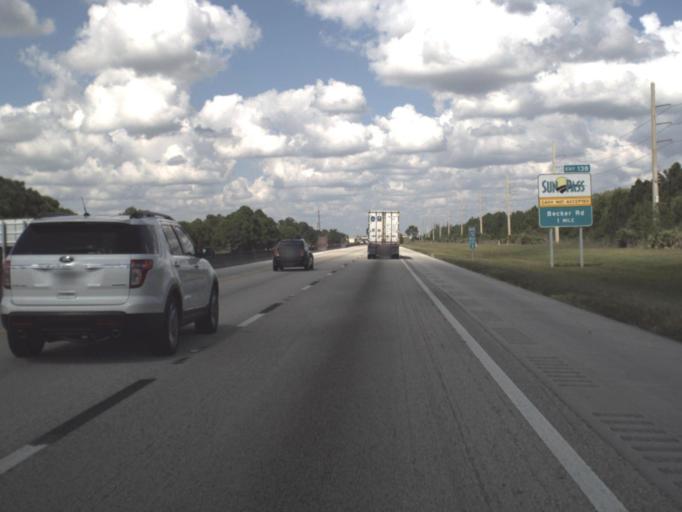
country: US
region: Florida
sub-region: Martin County
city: North River Shores
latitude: 27.1972
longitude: -80.3276
